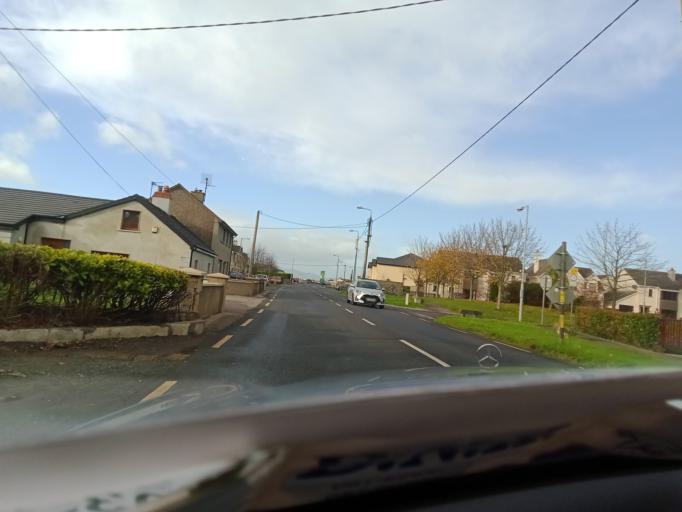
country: IE
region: Leinster
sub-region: Kilkenny
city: Piltown
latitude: 52.3323
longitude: -7.3150
